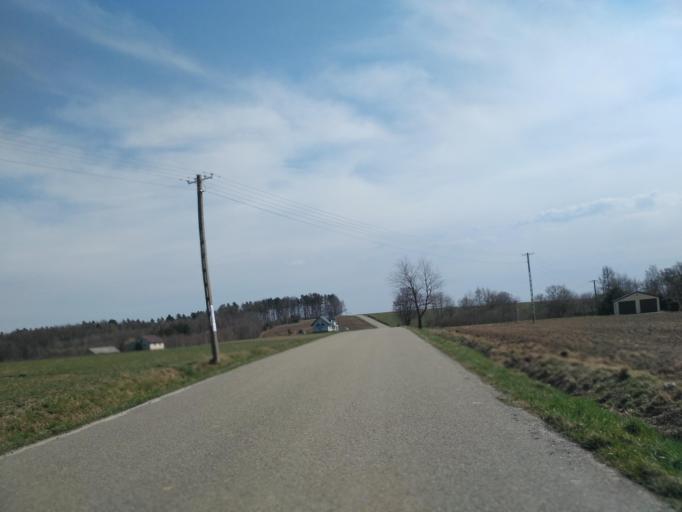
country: PL
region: Subcarpathian Voivodeship
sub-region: Powiat ropczycko-sedziszowski
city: Iwierzyce
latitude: 49.9747
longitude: 21.7485
